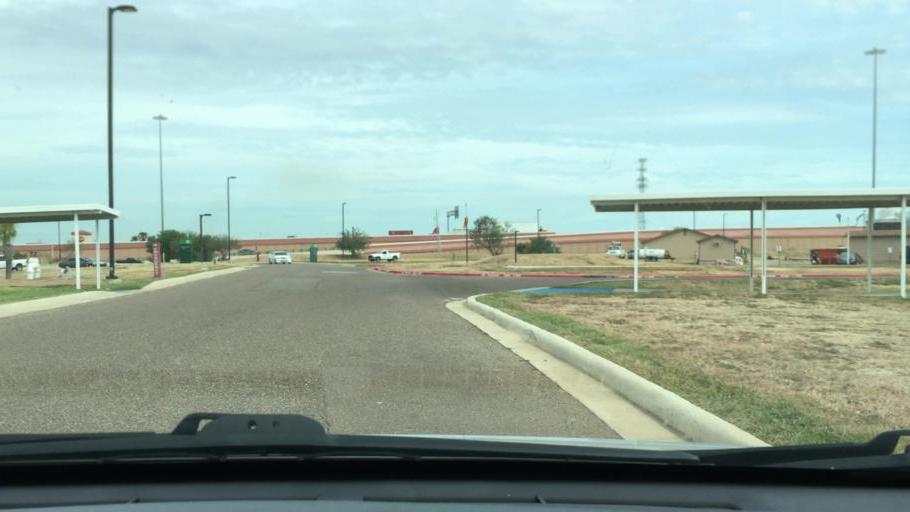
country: US
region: Texas
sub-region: Webb County
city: Laredo
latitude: 27.6062
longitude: -99.4794
